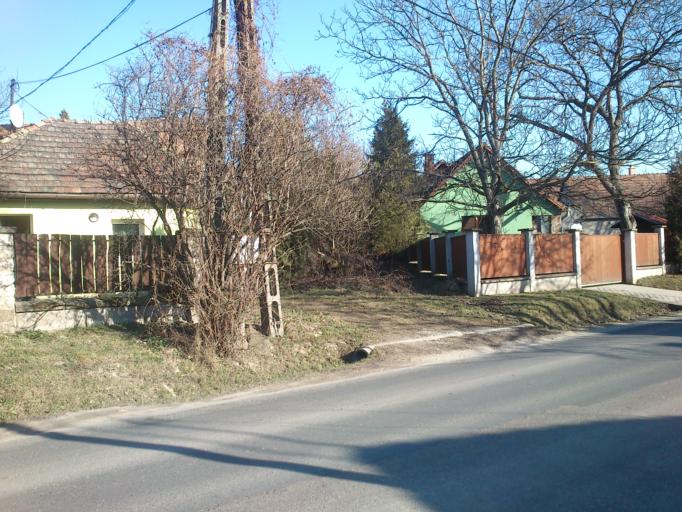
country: HU
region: Pest
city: Soskut
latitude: 47.4050
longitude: 18.8340
